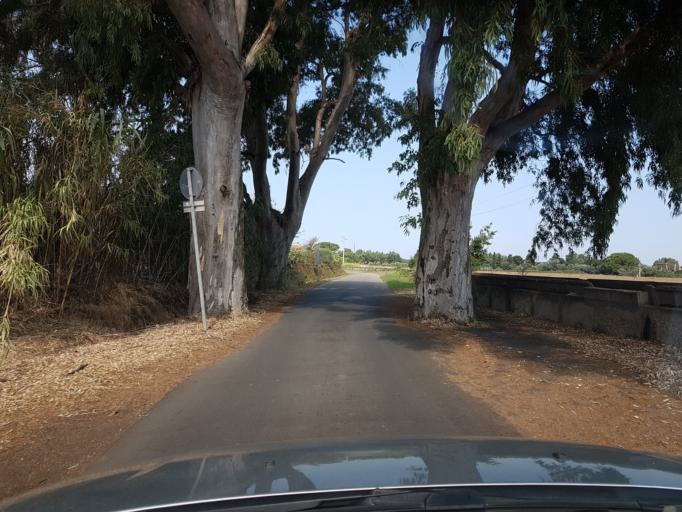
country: IT
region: Sardinia
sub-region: Provincia di Oristano
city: Donigala Fenugheddu
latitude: 39.9366
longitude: 8.5776
